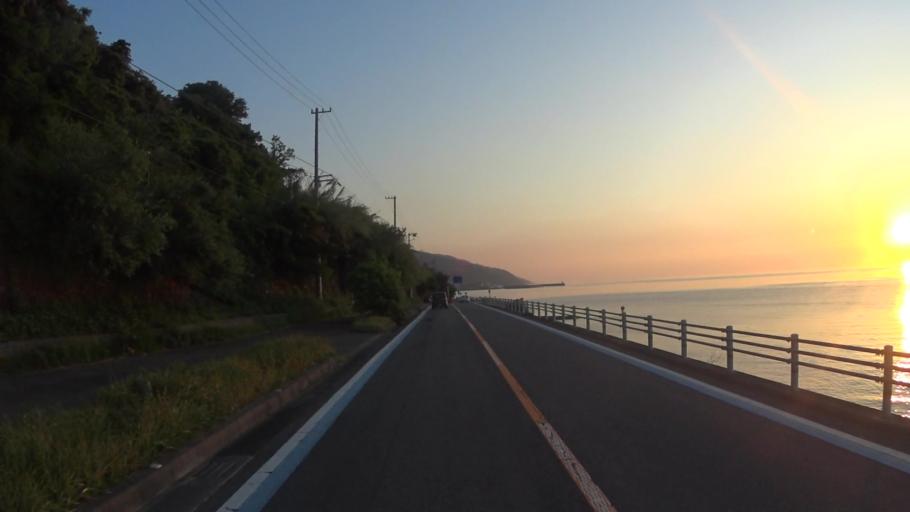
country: JP
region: Ehime
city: Iyo
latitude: 33.6588
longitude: 132.5943
